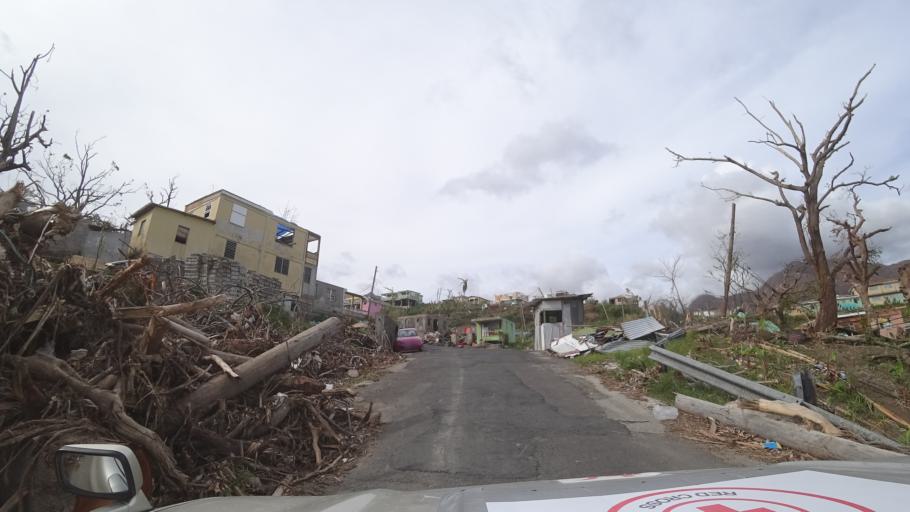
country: DM
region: Saint Patrick
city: Berekua
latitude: 15.2421
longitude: -61.3199
